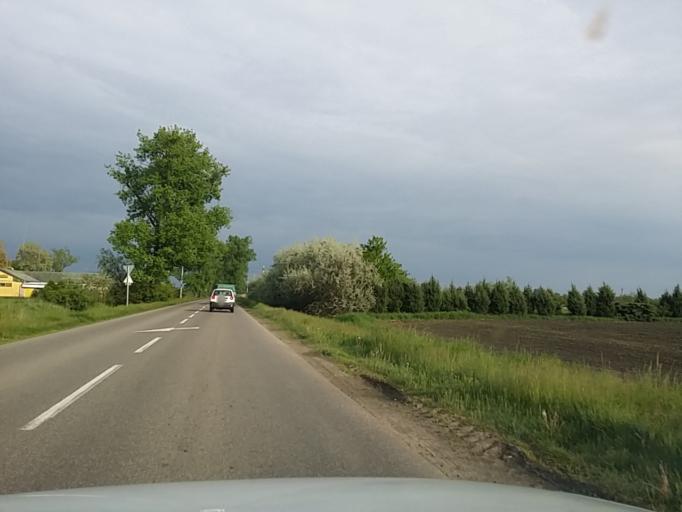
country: HU
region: Jasz-Nagykun-Szolnok
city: Jaszbereny
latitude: 47.5158
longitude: 19.8806
